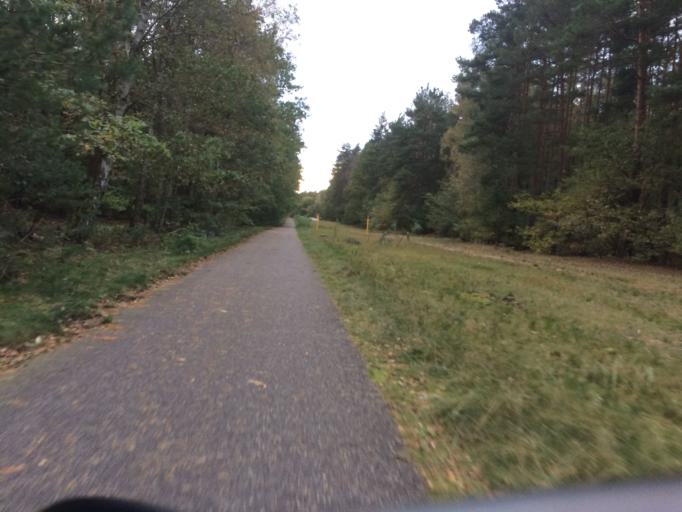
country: DE
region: Brandenburg
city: Birkenwerder
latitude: 52.7091
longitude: 13.2979
